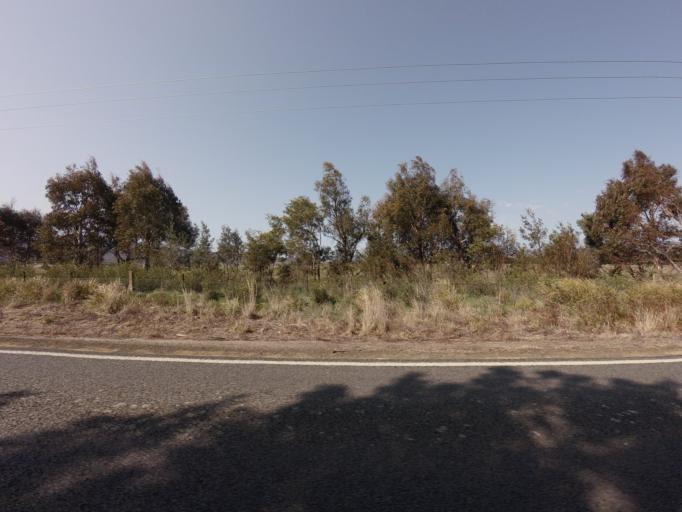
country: AU
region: Tasmania
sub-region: Northern Midlands
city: Evandale
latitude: -41.7932
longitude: 147.7098
